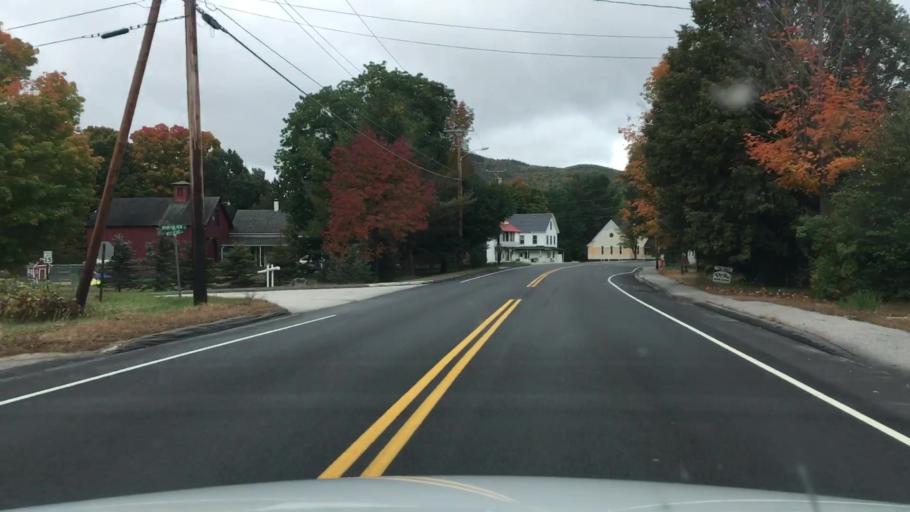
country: US
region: Maine
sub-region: Oxford County
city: Bethel
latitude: 44.4030
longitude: -70.8598
